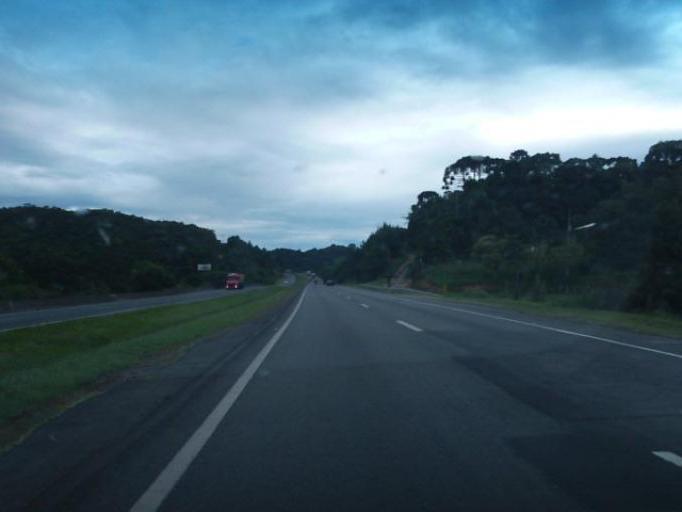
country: BR
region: Parana
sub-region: Campina Grande Do Sul
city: Campina Grande do Sul
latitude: -25.2242
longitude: -48.9064
